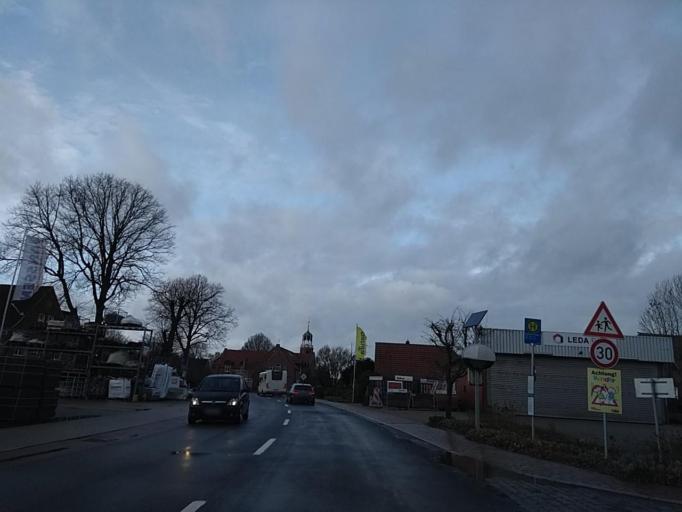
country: DE
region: Lower Saxony
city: Emden
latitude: 53.3146
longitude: 7.2832
